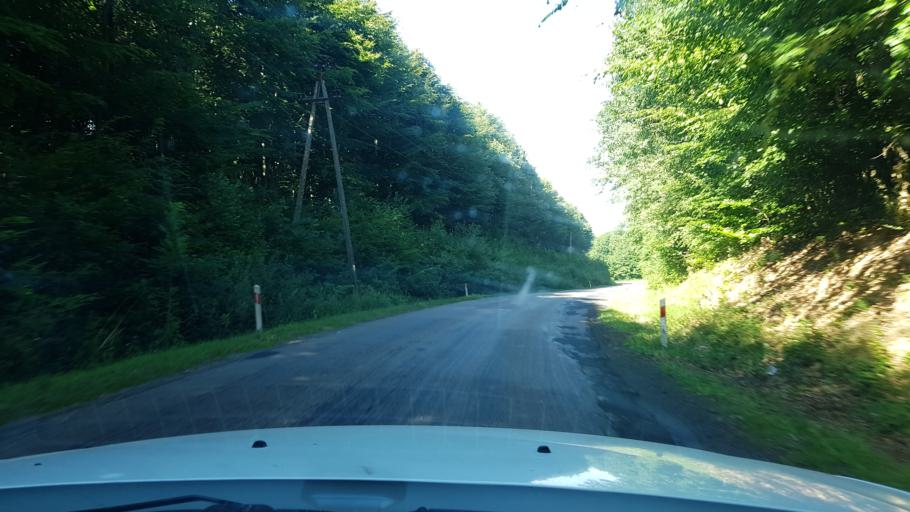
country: PL
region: West Pomeranian Voivodeship
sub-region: Powiat swidwinski
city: Polczyn-Zdroj
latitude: 53.7363
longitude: 16.0766
